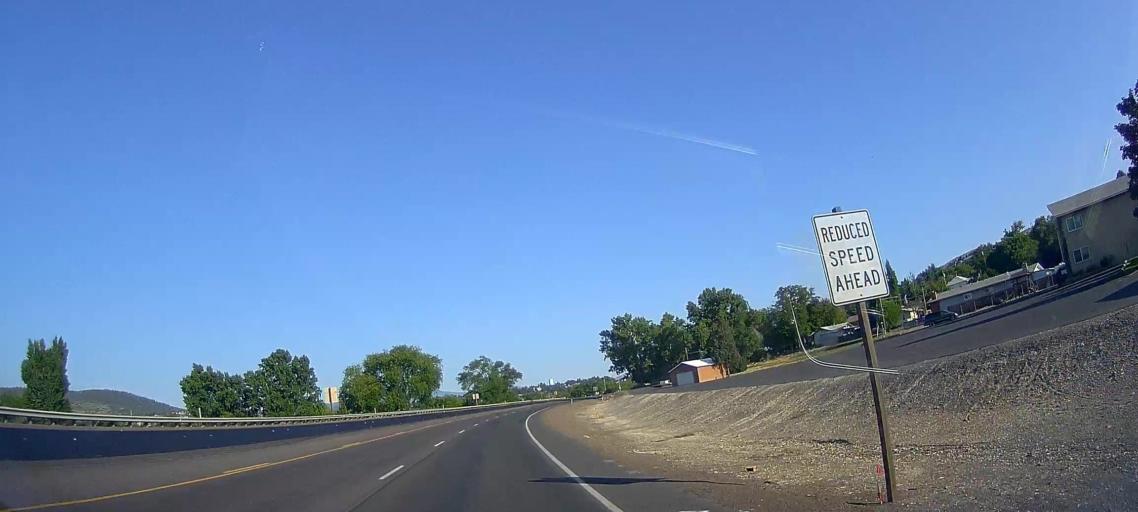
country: US
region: Oregon
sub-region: Klamath County
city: Klamath Falls
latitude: 42.2261
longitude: -121.7624
